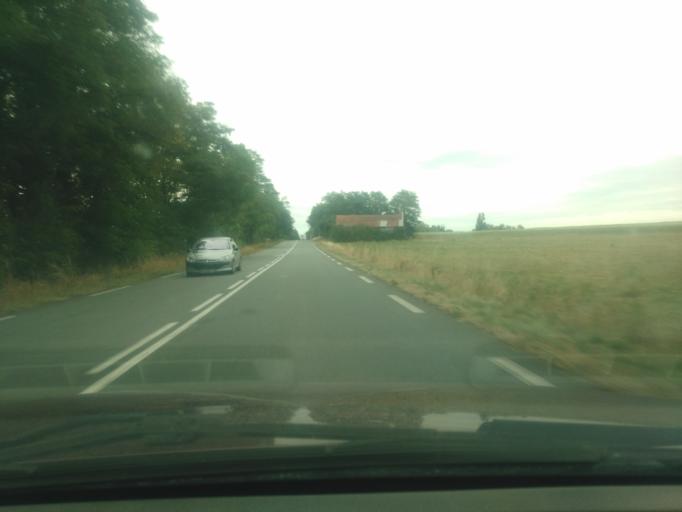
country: FR
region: Auvergne
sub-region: Departement de l'Allier
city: Ainay-le-Chateau
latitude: 46.7415
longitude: 2.7216
